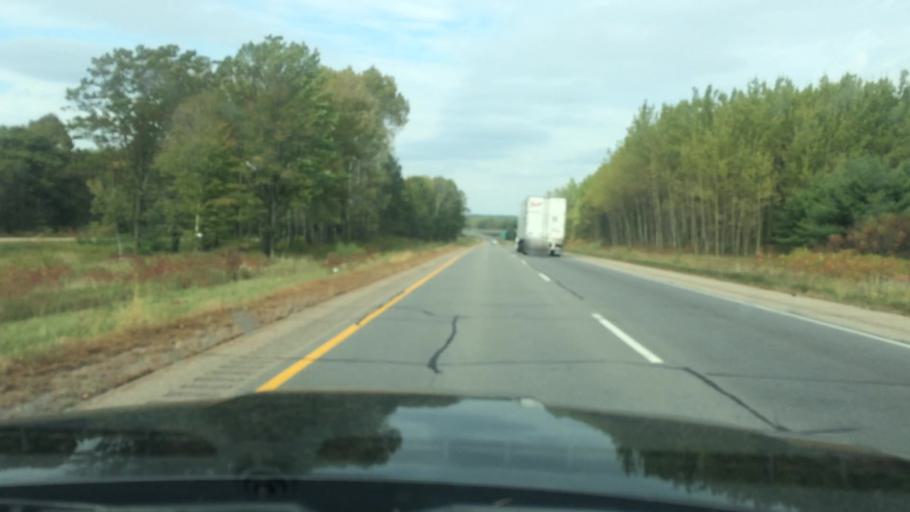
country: US
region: Wisconsin
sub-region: Marathon County
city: Mosinee
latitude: 44.7065
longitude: -89.6545
